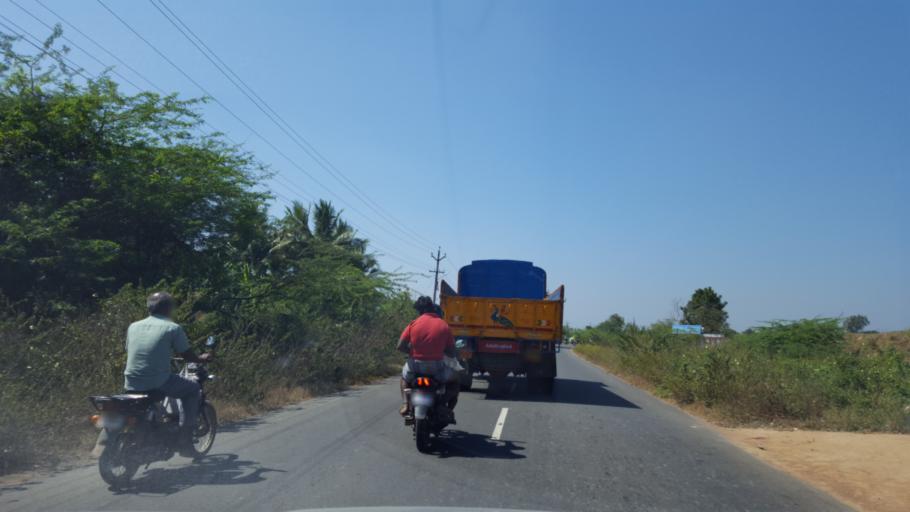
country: IN
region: Tamil Nadu
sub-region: Kancheepuram
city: Chengalpattu
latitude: 12.7387
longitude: 79.9408
